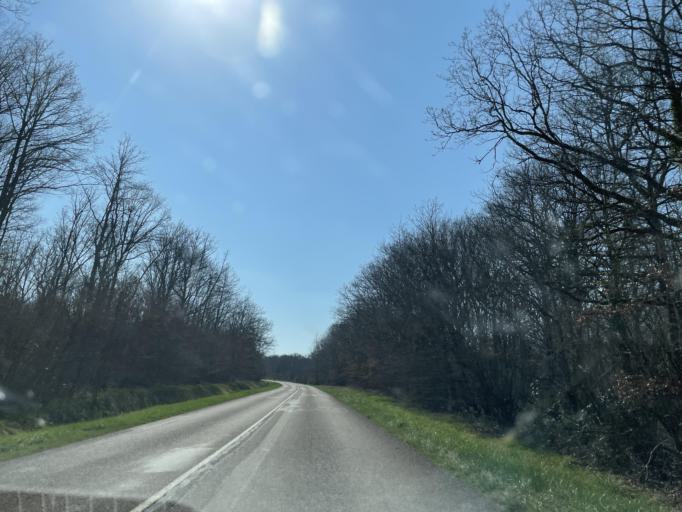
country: FR
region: Bourgogne
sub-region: Departement de la Cote-d'Or
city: Semur-en-Auxois
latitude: 47.4688
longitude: 4.3476
